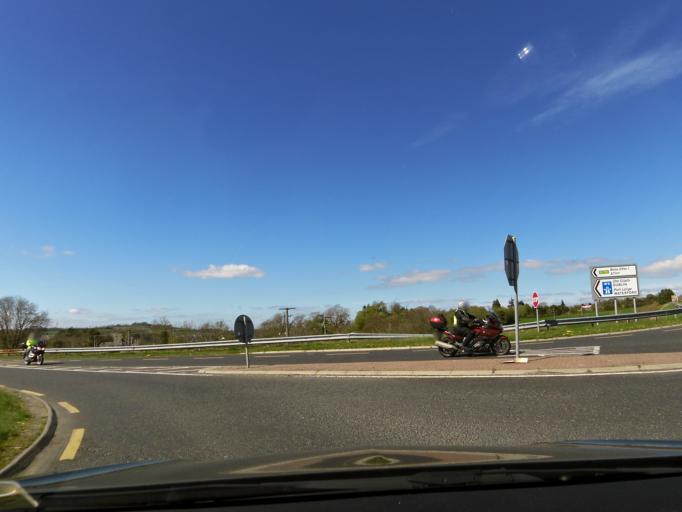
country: IE
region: Leinster
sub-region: Kildare
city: Moone
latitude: 53.0020
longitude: -6.8057
